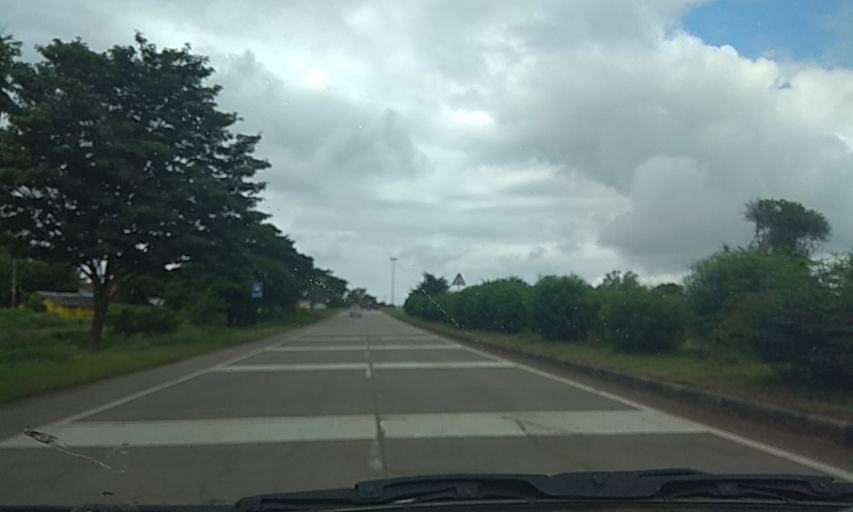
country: IN
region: Karnataka
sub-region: Belgaum
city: Sankeshwar
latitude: 16.3193
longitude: 74.4234
